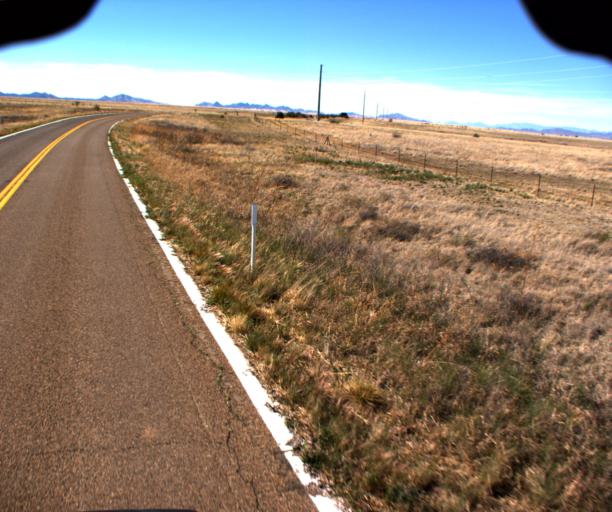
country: US
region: Arizona
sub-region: Cochise County
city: Huachuca City
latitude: 31.6218
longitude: -110.5900
